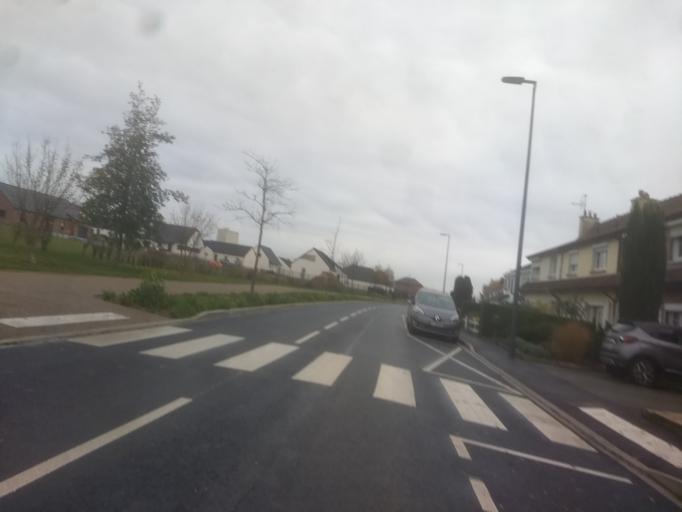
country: FR
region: Nord-Pas-de-Calais
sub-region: Departement du Pas-de-Calais
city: Dainville
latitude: 50.2875
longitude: 2.7303
